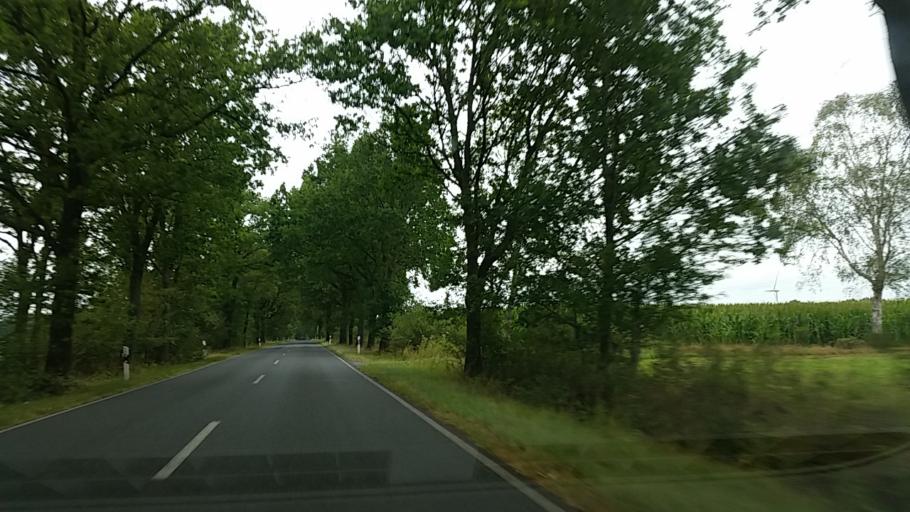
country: DE
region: Lower Saxony
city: Vollersode
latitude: 53.4051
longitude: 8.9194
